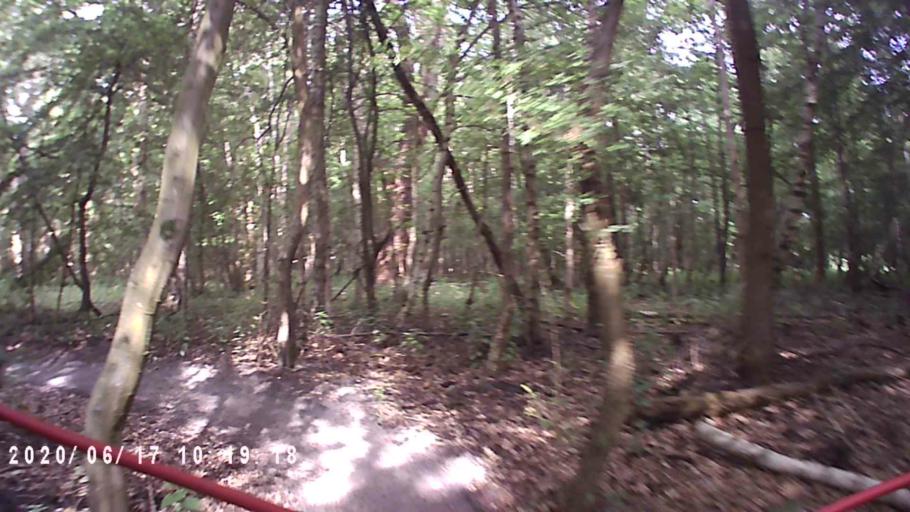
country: NL
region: Groningen
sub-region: Gemeente De Marne
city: Ulrum
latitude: 53.3888
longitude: 6.2511
